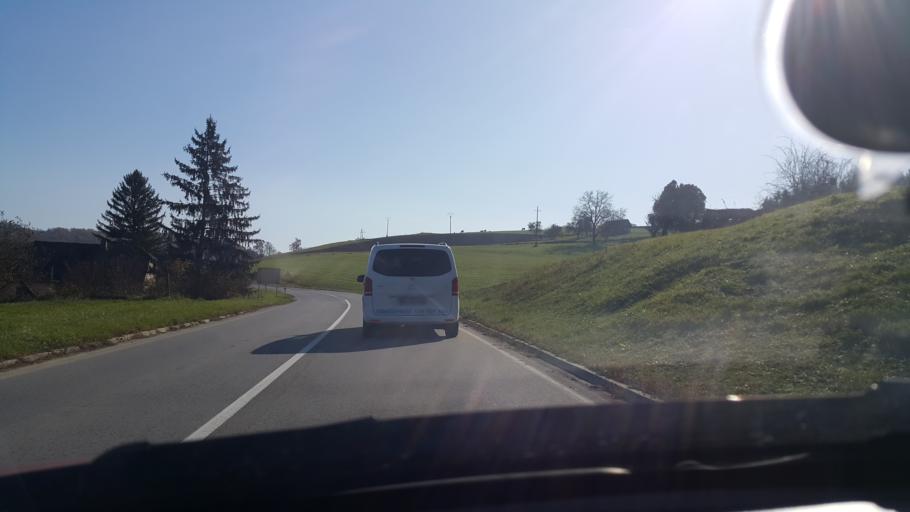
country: SI
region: Bistrica ob Sotli
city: Bistrica ob Sotli
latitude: 46.0872
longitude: 15.6234
